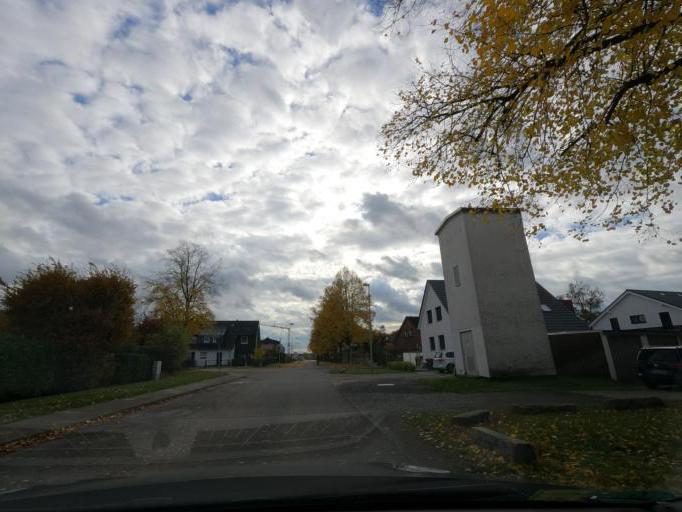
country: DE
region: Lower Saxony
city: Leiferde
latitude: 52.2070
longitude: 10.5225
